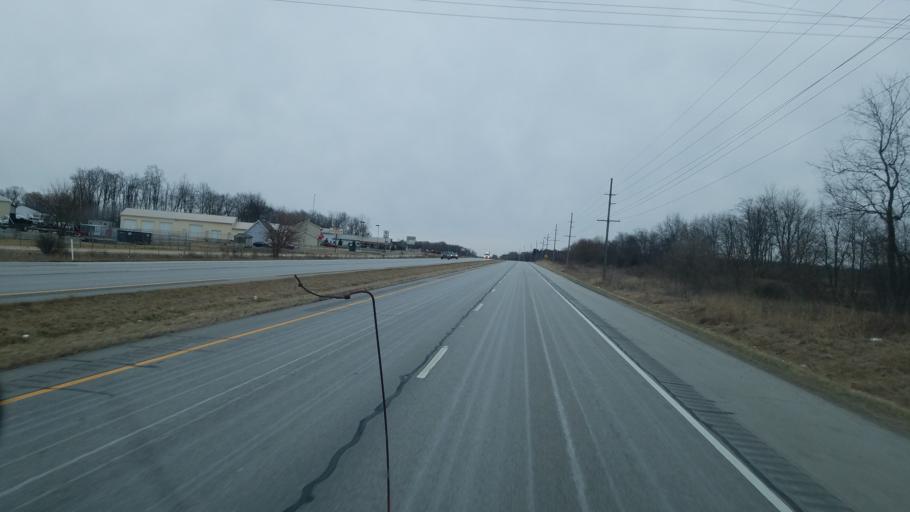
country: US
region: Indiana
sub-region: Porter County
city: Valparaiso
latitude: 41.4444
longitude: -86.9953
